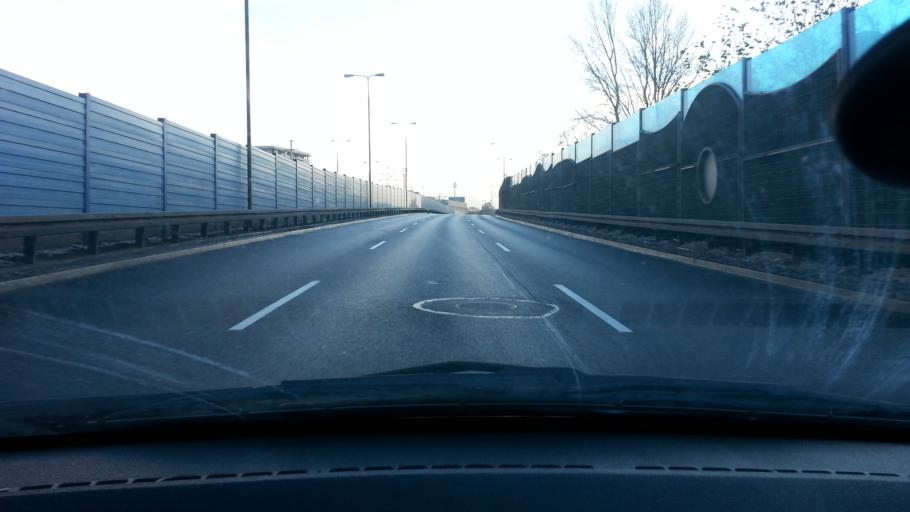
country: PL
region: Masovian Voivodeship
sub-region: Warszawa
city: Wola
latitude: 52.2487
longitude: 20.9567
